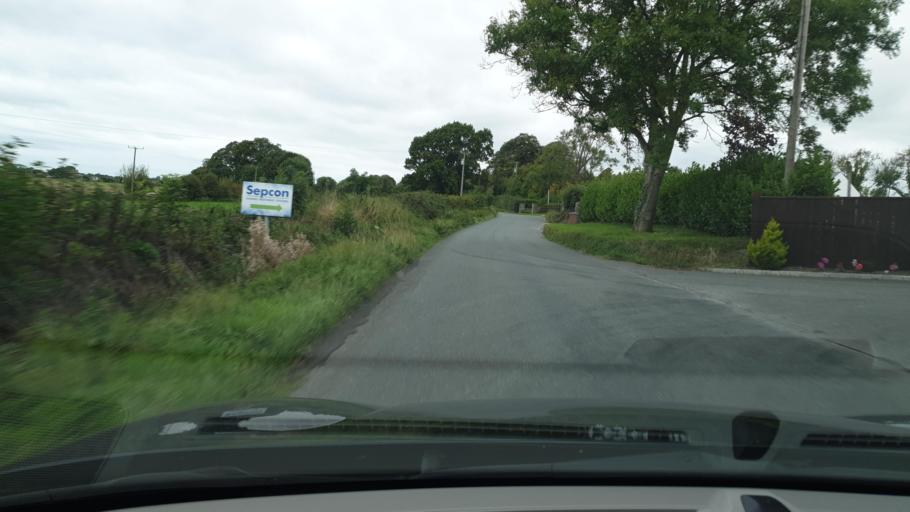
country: IE
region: Leinster
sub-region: Kildare
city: Kilcock
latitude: 53.3984
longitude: -6.6385
